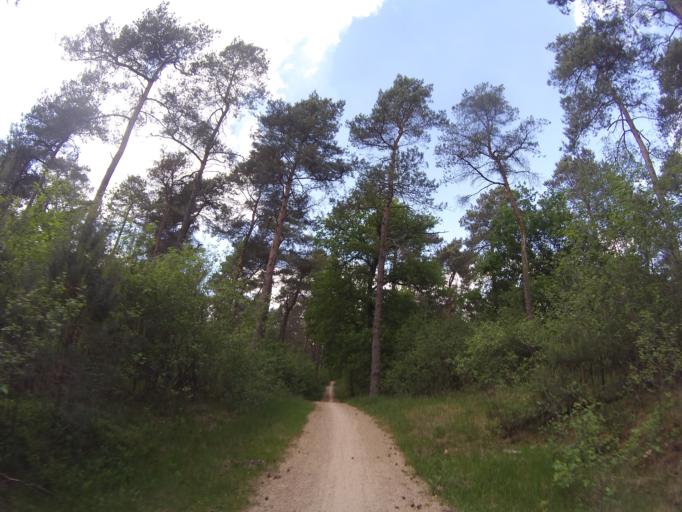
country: NL
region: Gelderland
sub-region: Gemeente Barneveld
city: Stroe
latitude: 52.1695
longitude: 5.7176
